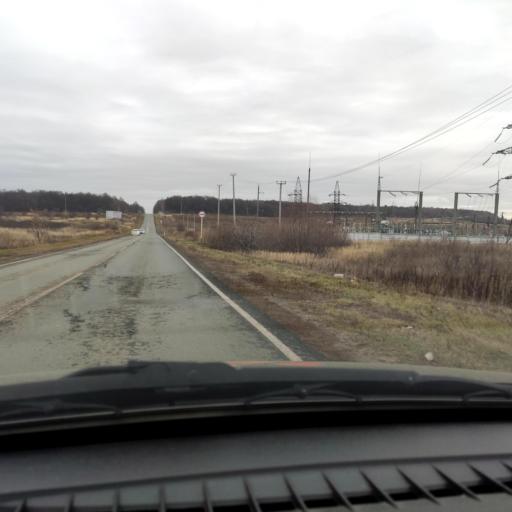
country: RU
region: Samara
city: Zhigulevsk
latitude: 53.3401
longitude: 49.4767
